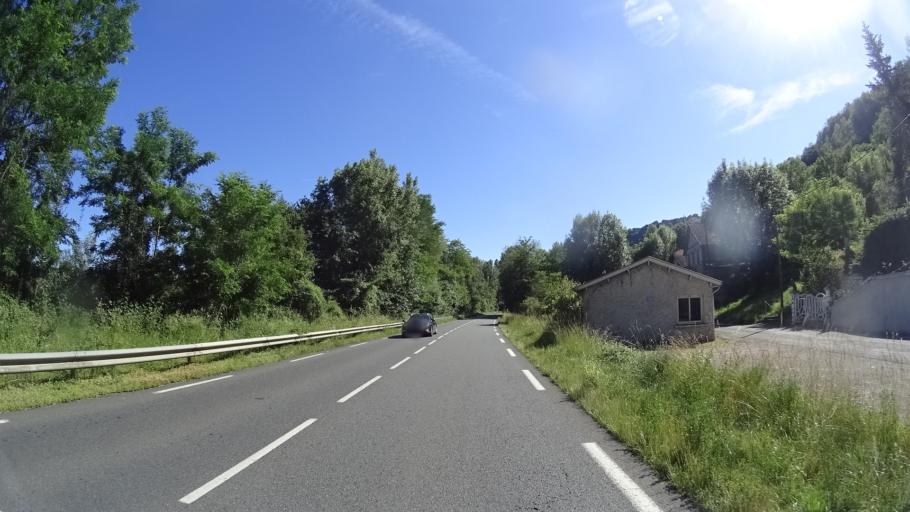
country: FR
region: Midi-Pyrenees
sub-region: Departement de l'Aveyron
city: Capdenac-Gare
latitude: 44.5846
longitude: 2.0775
